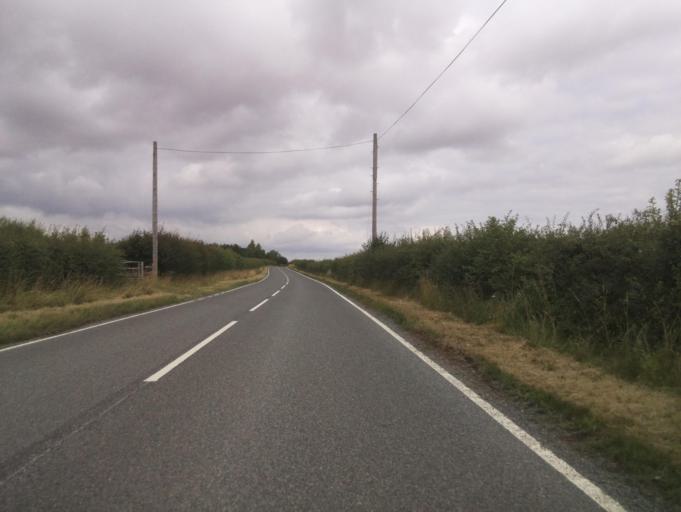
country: GB
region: England
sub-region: District of Rutland
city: Tickencote
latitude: 52.6777
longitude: -0.5124
